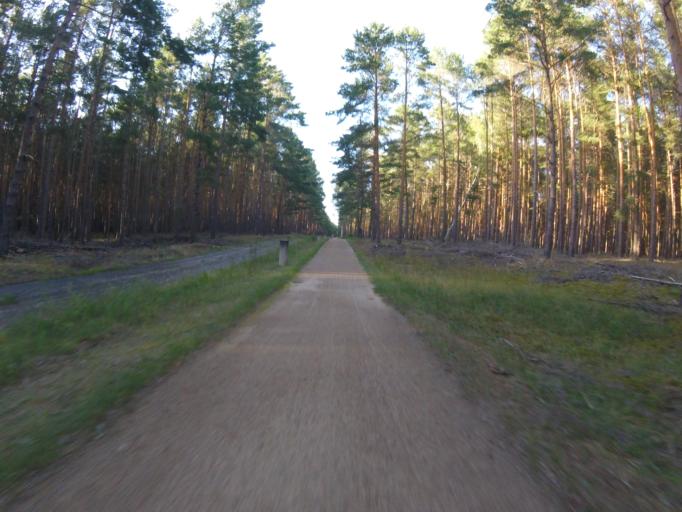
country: DE
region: Brandenburg
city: Munchehofe
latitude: 52.1993
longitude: 13.7655
